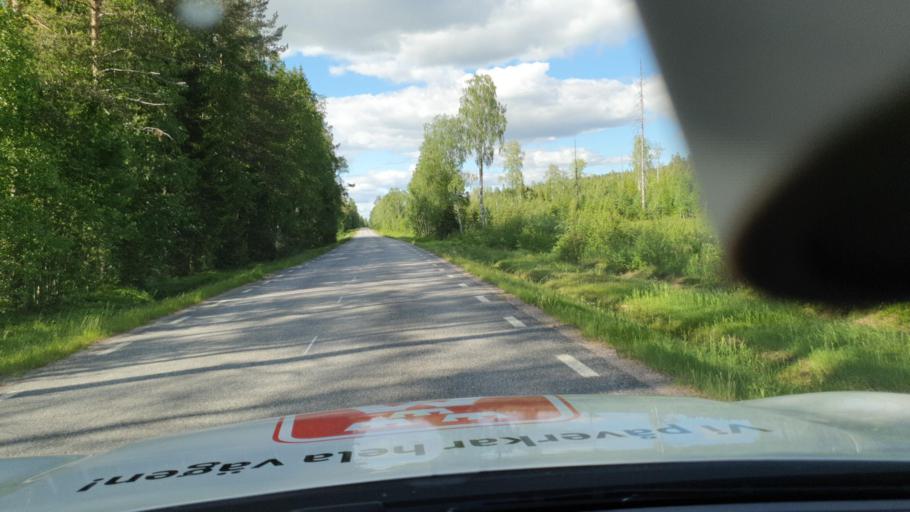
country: SE
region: Vaesterbotten
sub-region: Vannas Kommun
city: Vannasby
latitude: 63.8147
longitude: 19.8563
